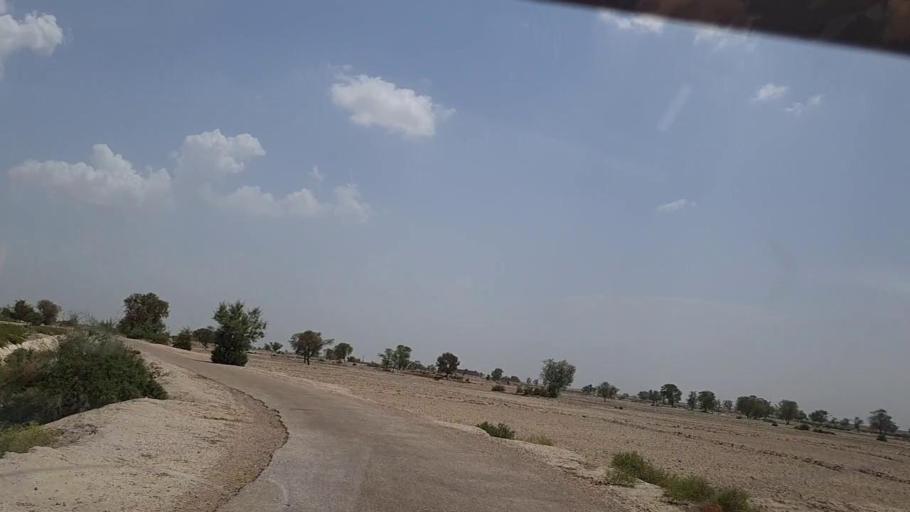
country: PK
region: Sindh
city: Bhan
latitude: 26.5331
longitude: 67.6324
